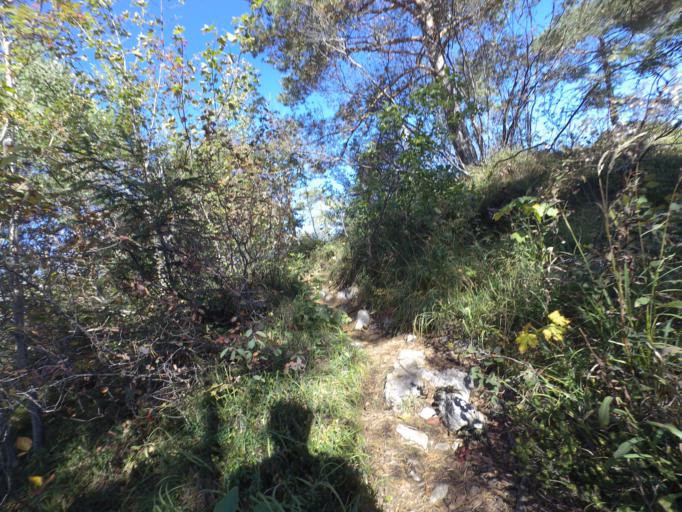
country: AT
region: Salzburg
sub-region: Politischer Bezirk Hallein
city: Hallein
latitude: 47.6910
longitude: 13.0750
